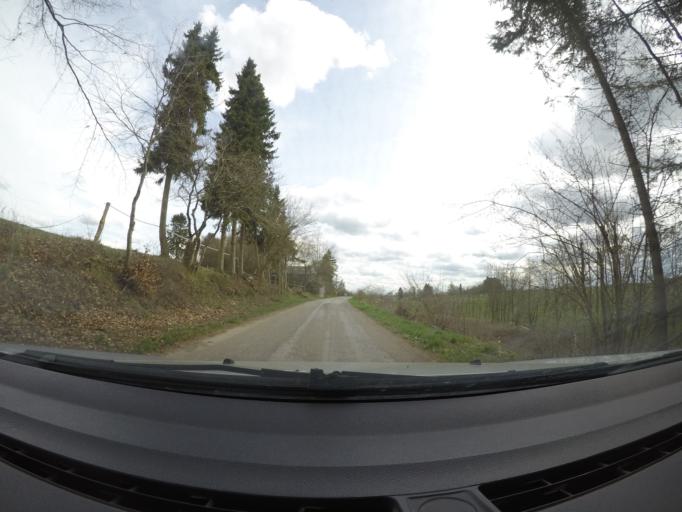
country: BE
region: Wallonia
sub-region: Province du Luxembourg
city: Neufchateau
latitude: 49.8152
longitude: 5.4759
